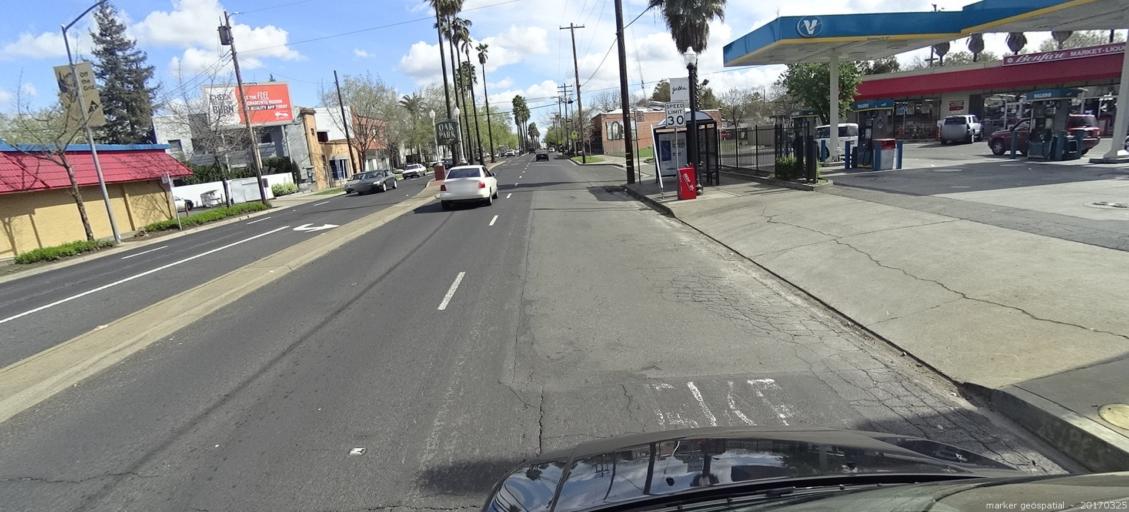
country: US
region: California
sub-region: Sacramento County
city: Sacramento
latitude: 38.5559
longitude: -121.4724
